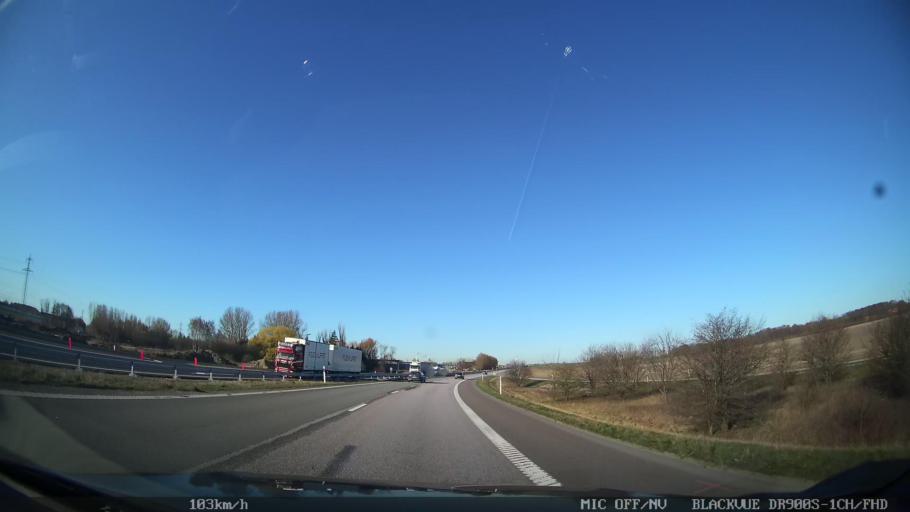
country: SE
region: Skane
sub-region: Burlovs Kommun
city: Arloev
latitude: 55.6514
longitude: 13.0955
